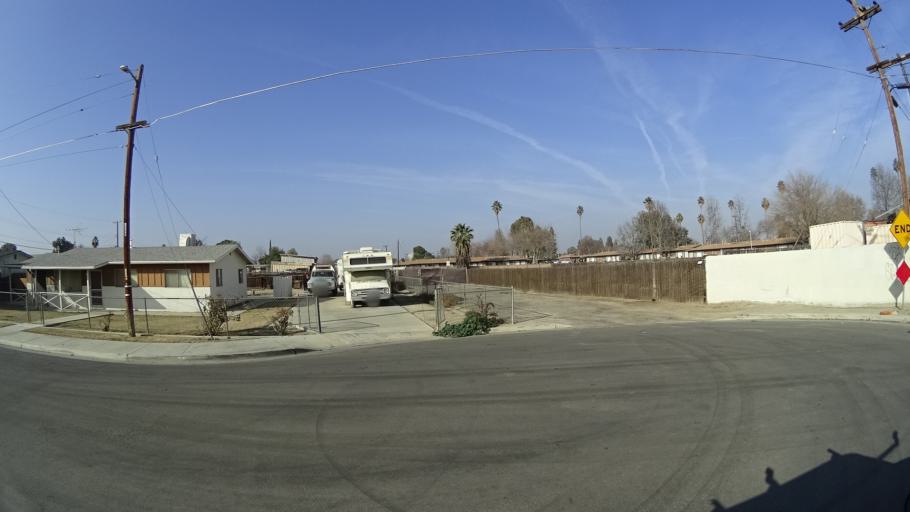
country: US
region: California
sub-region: Kern County
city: Bakersfield
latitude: 35.3297
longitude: -119.0233
